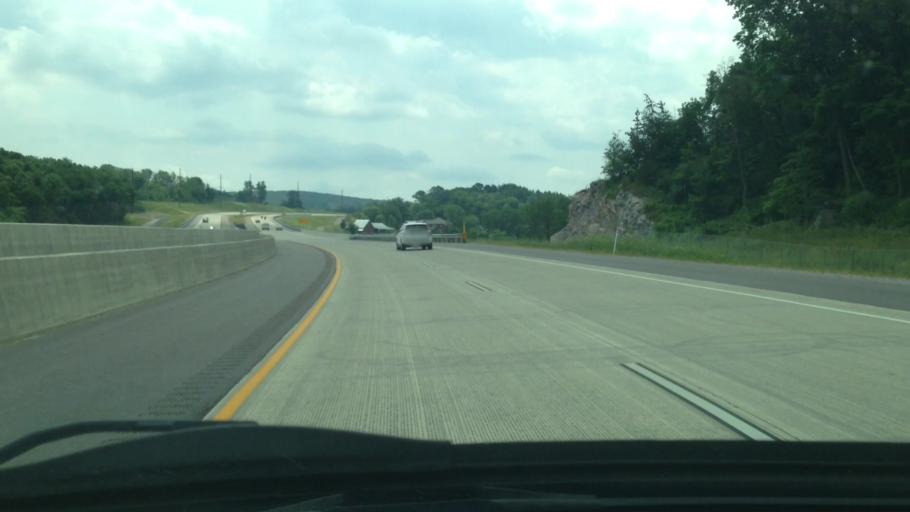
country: US
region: Wisconsin
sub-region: Sauk County
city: West Baraboo
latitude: 43.4341
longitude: -89.7776
